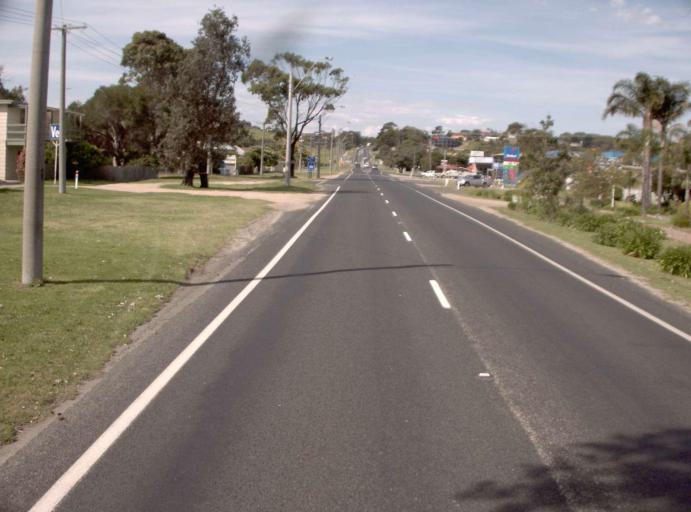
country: AU
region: Victoria
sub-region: East Gippsland
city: Lakes Entrance
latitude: -37.8756
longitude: 148.0068
